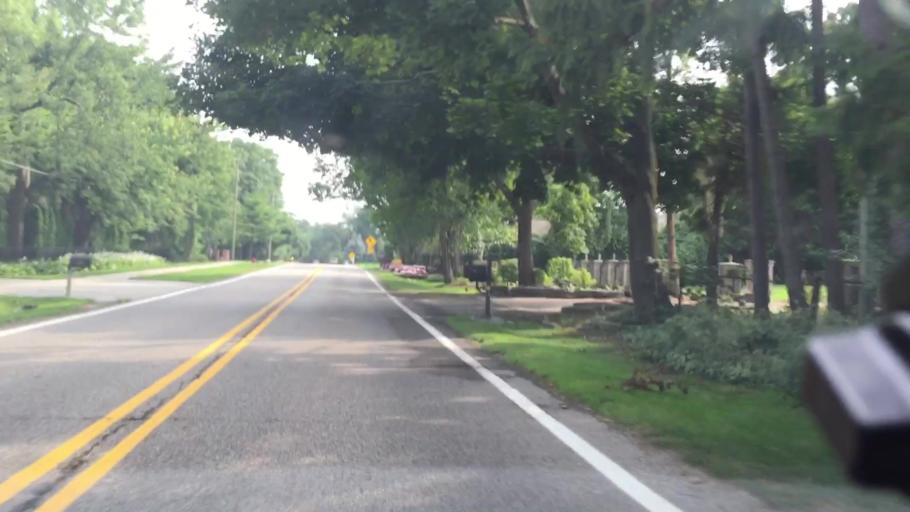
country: US
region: Michigan
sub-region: Oakland County
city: Bloomfield Hills
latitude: 42.5889
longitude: -83.2869
